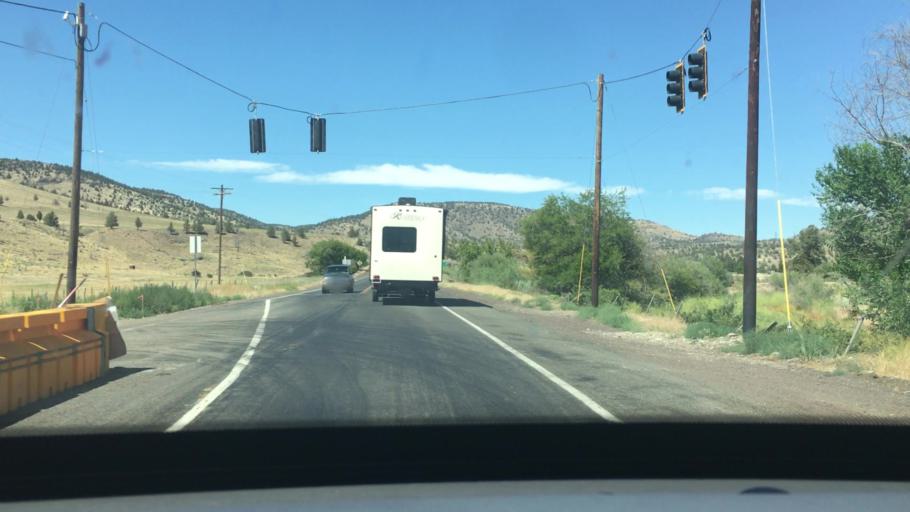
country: US
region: Oregon
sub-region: Jefferson County
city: Madras
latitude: 44.8132
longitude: -120.9322
